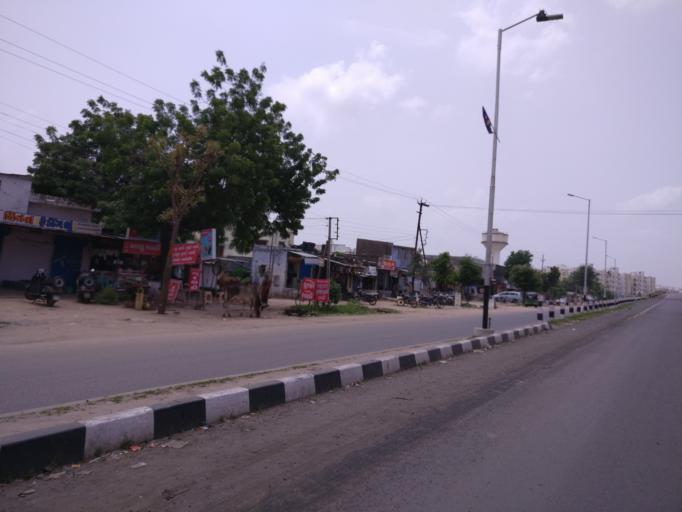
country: IN
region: Gujarat
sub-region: Mahesana
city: Jhulasan
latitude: 23.2396
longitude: 72.4904
